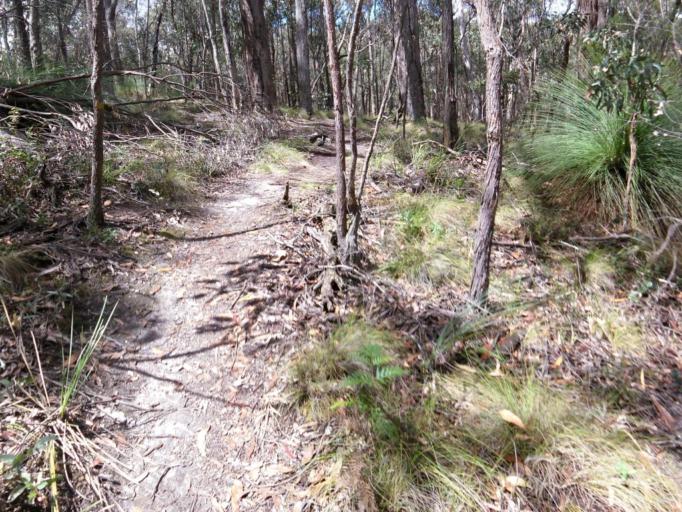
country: AU
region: Victoria
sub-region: Melton
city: Melton West
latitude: -37.4895
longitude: 144.5406
